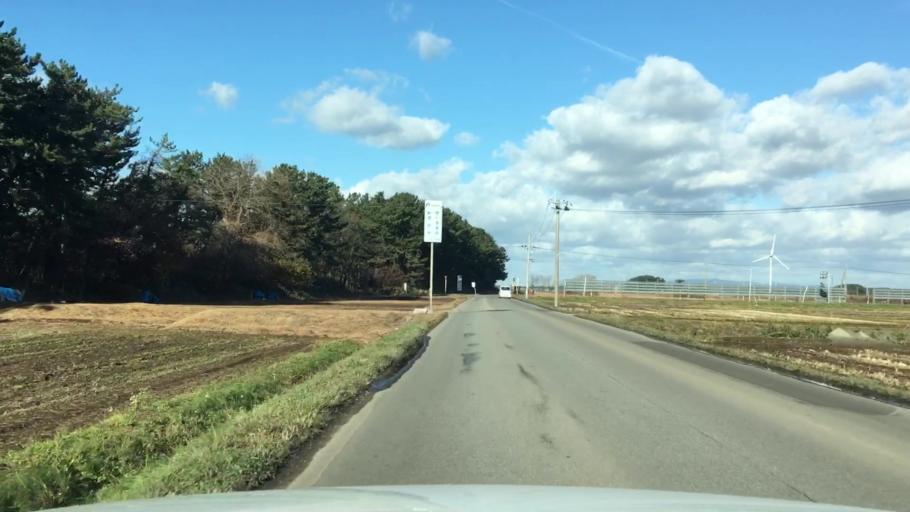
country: JP
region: Aomori
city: Shimokizukuri
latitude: 40.8477
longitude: 140.2998
